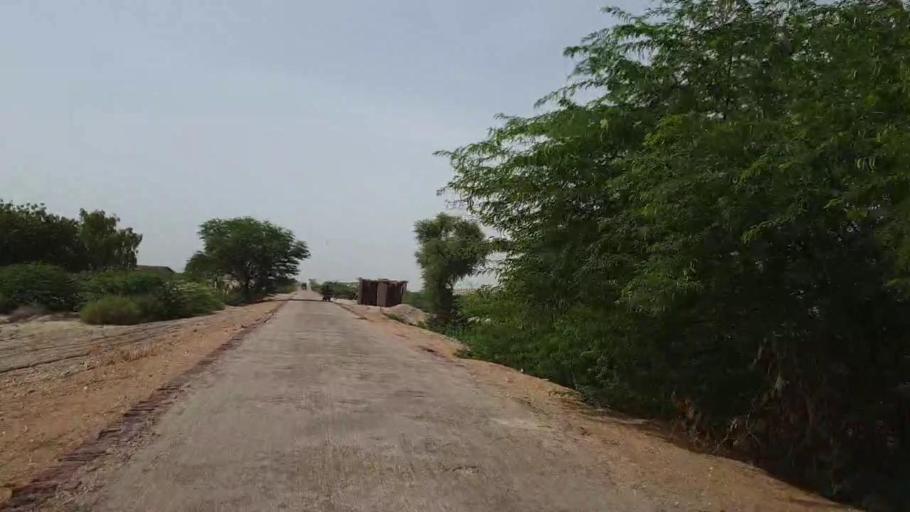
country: PK
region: Sindh
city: Bandhi
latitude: 26.5534
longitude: 68.3835
